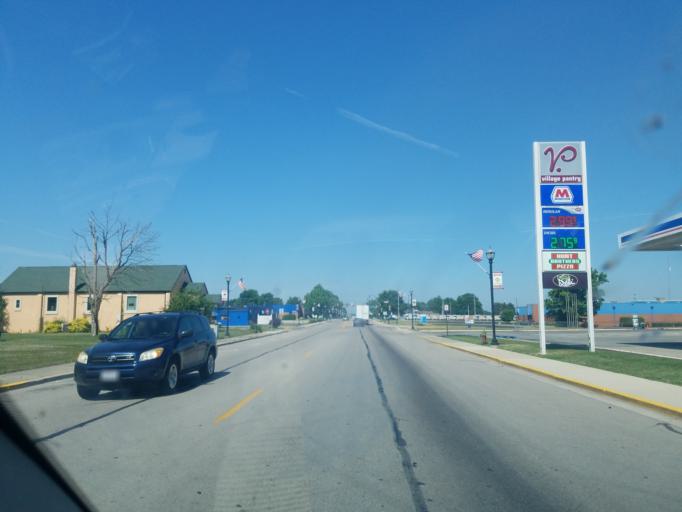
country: US
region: Ohio
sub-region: Shelby County
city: Jackson Center
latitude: 40.4399
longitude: -84.0438
